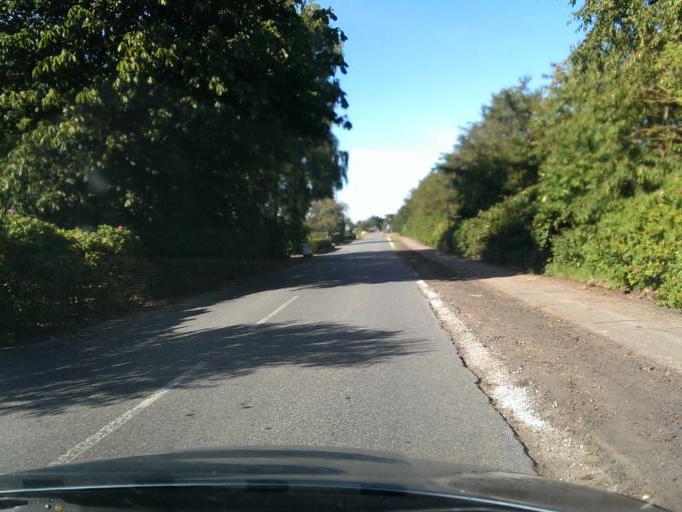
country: DK
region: Central Jutland
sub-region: Odder Kommune
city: Odder
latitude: 55.9149
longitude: 10.1410
